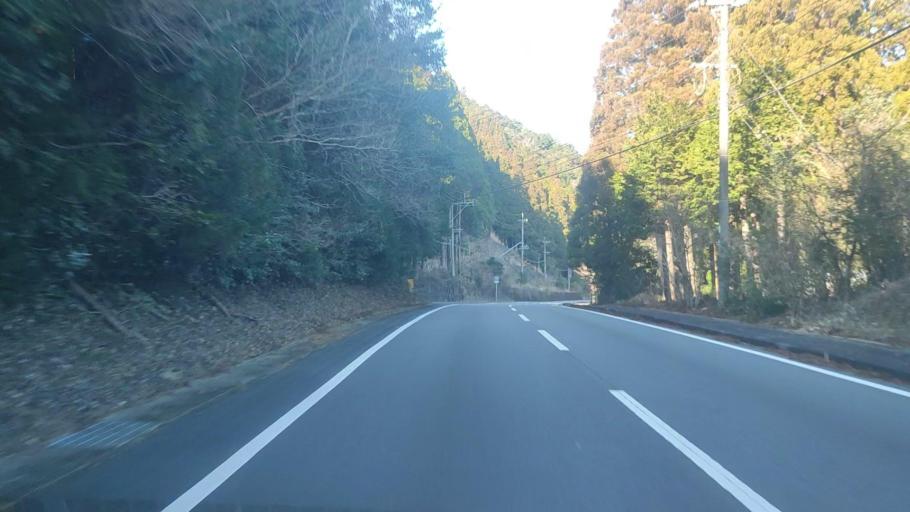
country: JP
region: Oita
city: Saiki
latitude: 32.7419
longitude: 131.8233
